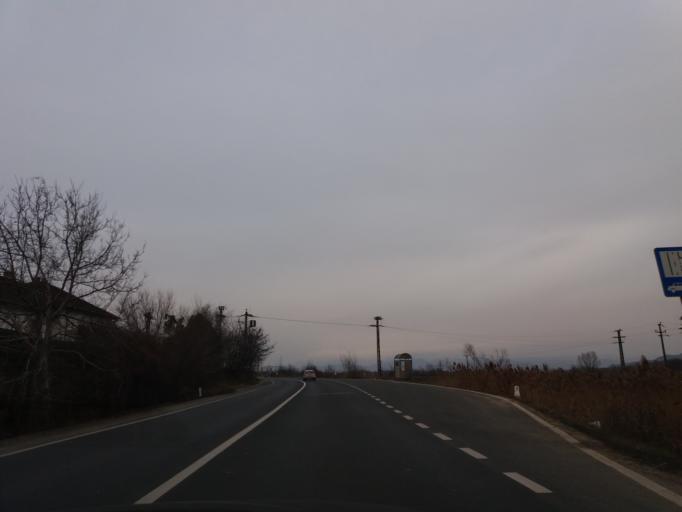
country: RO
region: Hunedoara
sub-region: Comuna Calan
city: Calan
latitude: 45.7589
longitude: 23.0010
